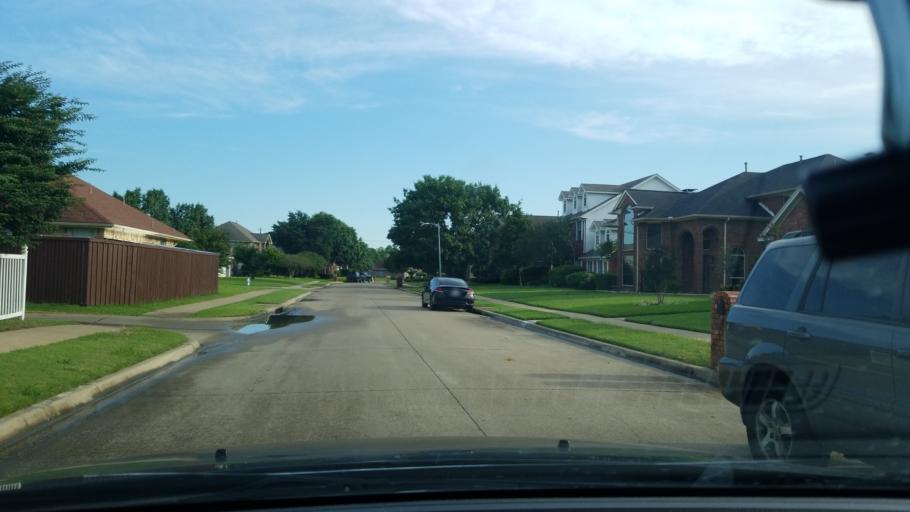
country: US
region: Texas
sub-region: Dallas County
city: Mesquite
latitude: 32.7961
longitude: -96.6052
